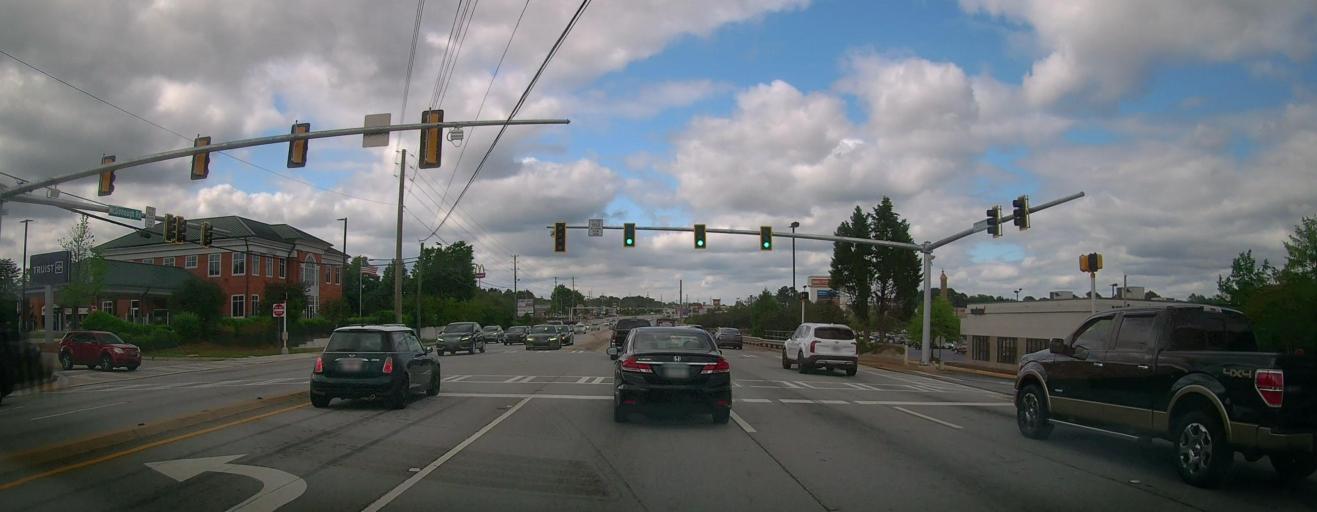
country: US
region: Georgia
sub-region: Rockdale County
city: Conyers
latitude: 33.6398
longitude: -84.0144
